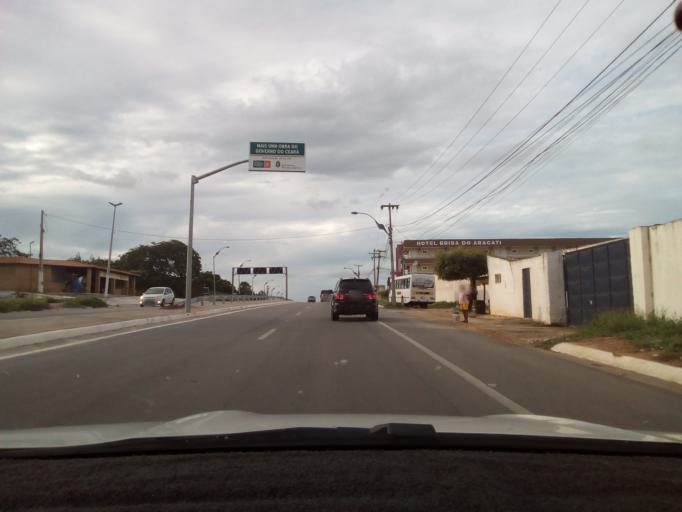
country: BR
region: Ceara
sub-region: Aracati
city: Aracati
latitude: -4.5747
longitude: -37.7913
